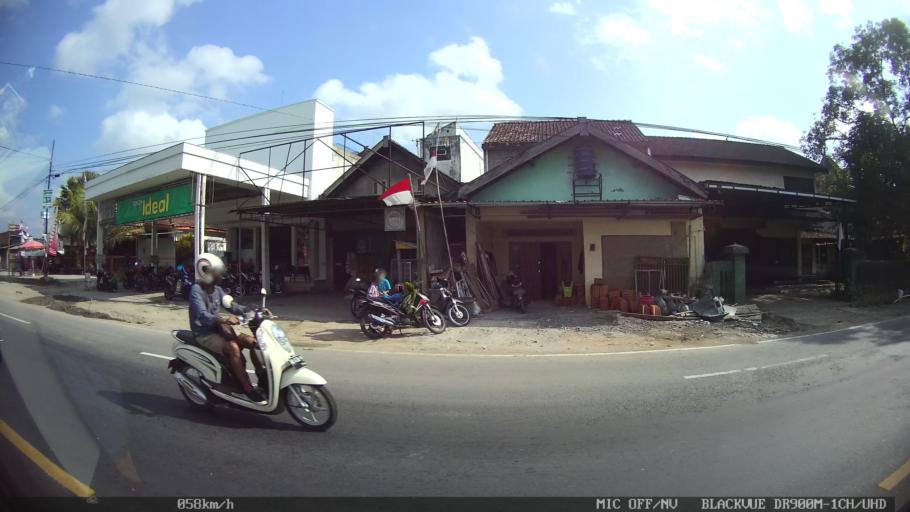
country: ID
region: Daerah Istimewa Yogyakarta
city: Godean
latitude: -7.8135
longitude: 110.2579
